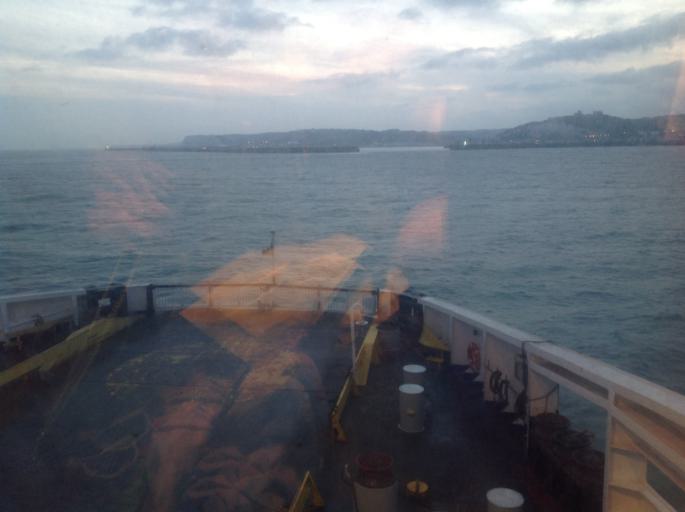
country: GB
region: England
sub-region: Kent
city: Dover
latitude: 51.1199
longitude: 1.3637
